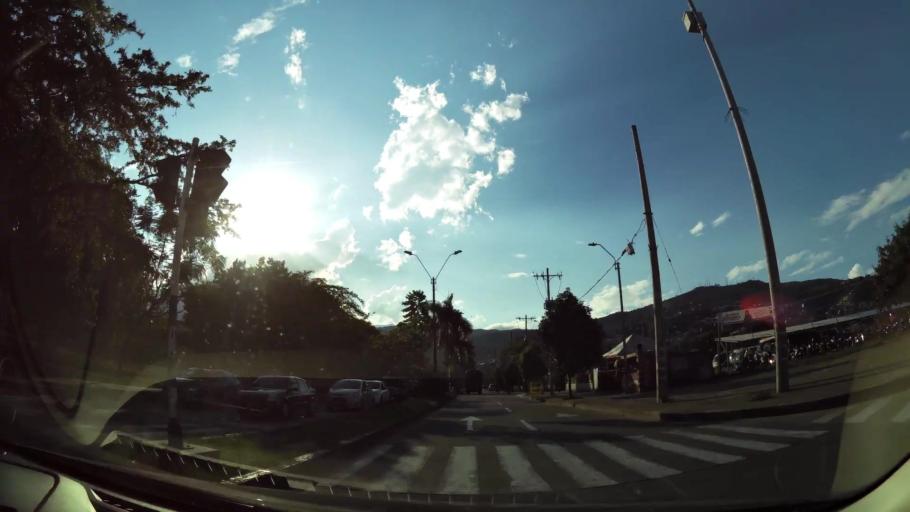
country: CO
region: Valle del Cauca
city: Cali
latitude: 3.4146
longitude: -76.5499
